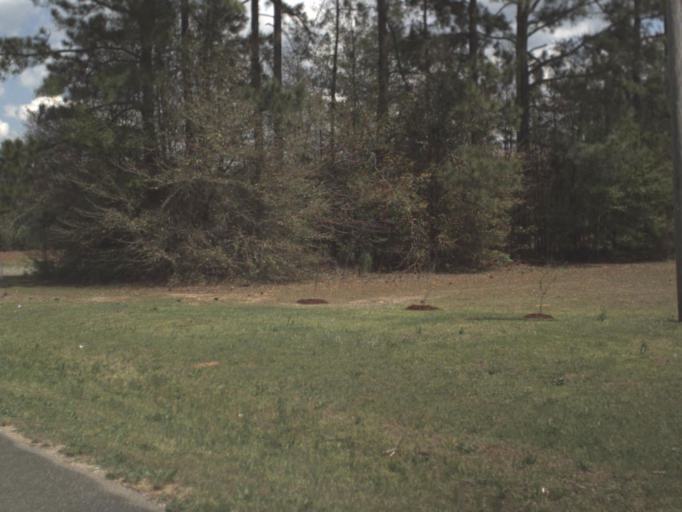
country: US
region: Florida
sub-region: Okaloosa County
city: Crestview
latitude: 30.8434
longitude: -86.6752
